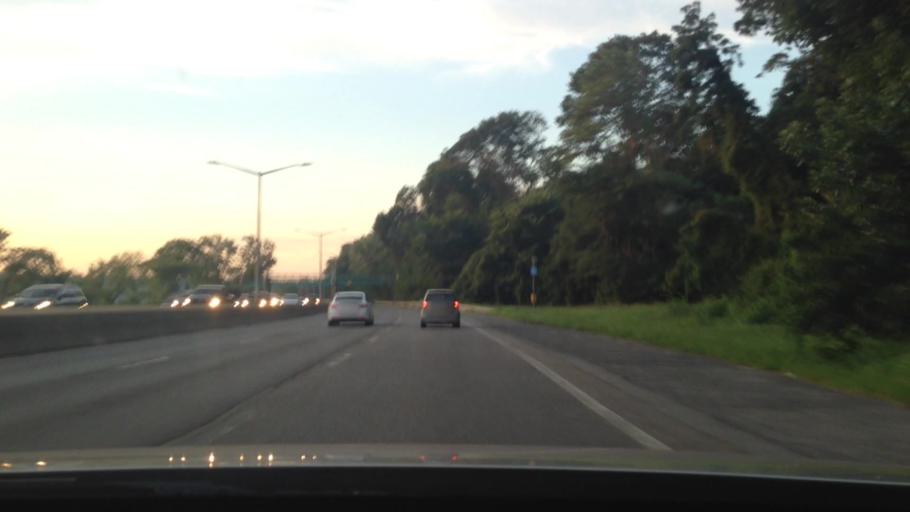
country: US
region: New York
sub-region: Nassau County
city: East Atlantic Beach
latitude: 40.7736
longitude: -73.7655
